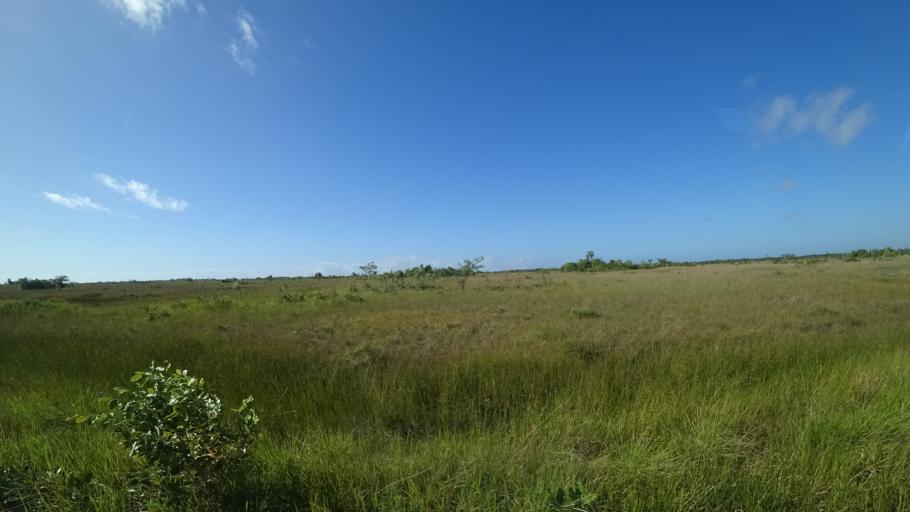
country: MZ
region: Sofala
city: Beira
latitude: -19.6992
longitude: 35.0287
